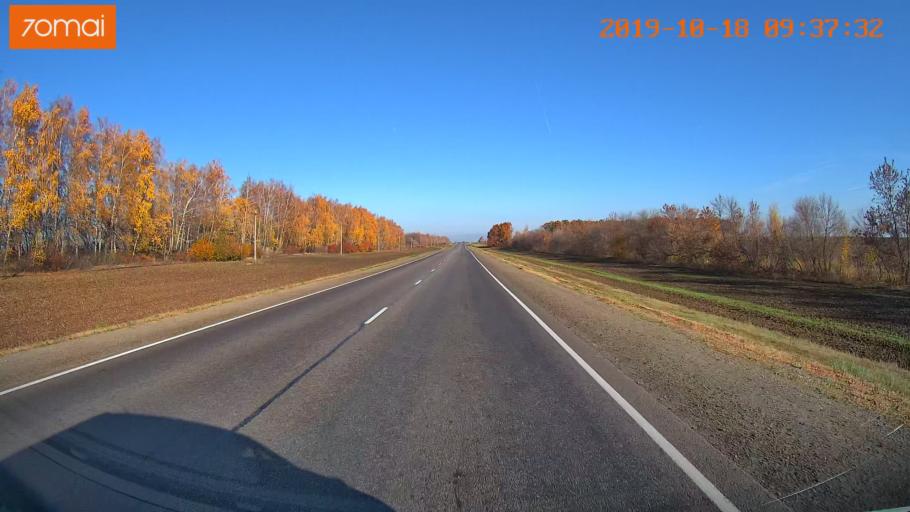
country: RU
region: Tula
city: Yefremov
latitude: 53.2238
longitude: 38.1407
